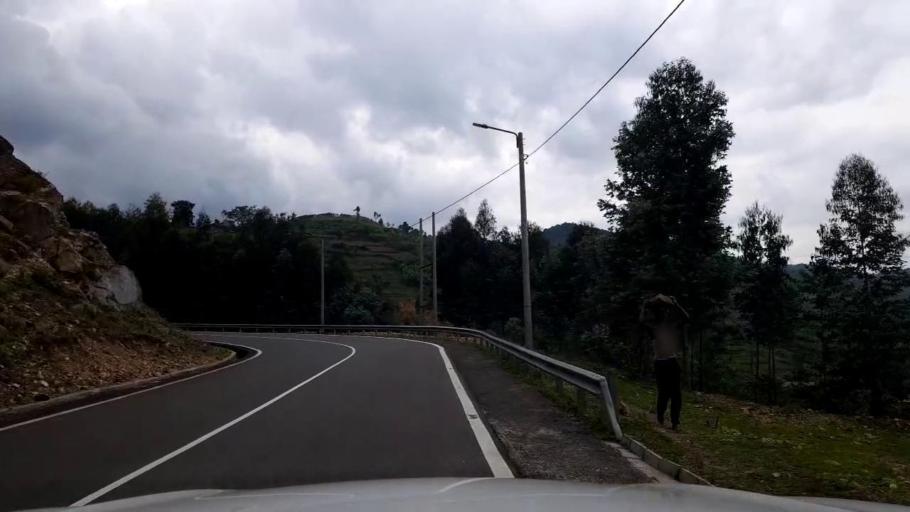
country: RW
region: Western Province
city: Kibuye
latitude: -1.9311
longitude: 29.3756
